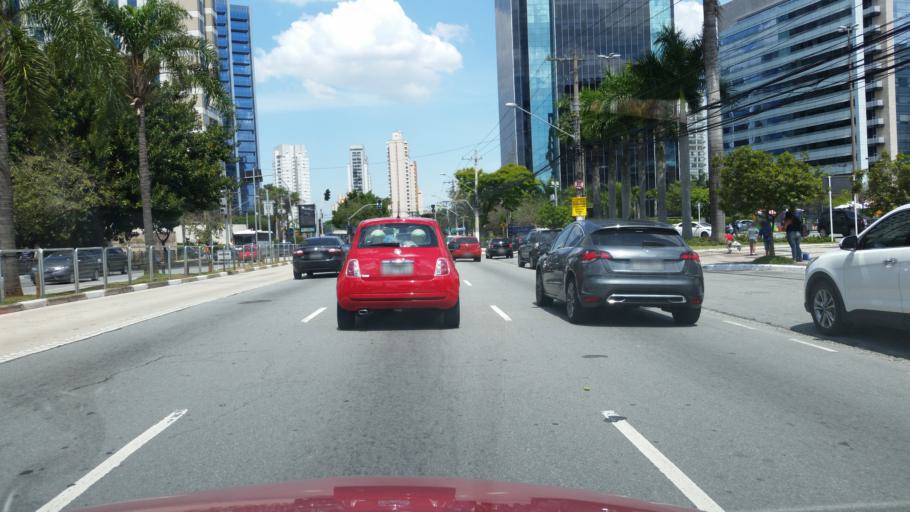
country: BR
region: Sao Paulo
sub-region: Taboao Da Serra
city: Taboao da Serra
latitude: -23.6223
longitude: -46.6976
